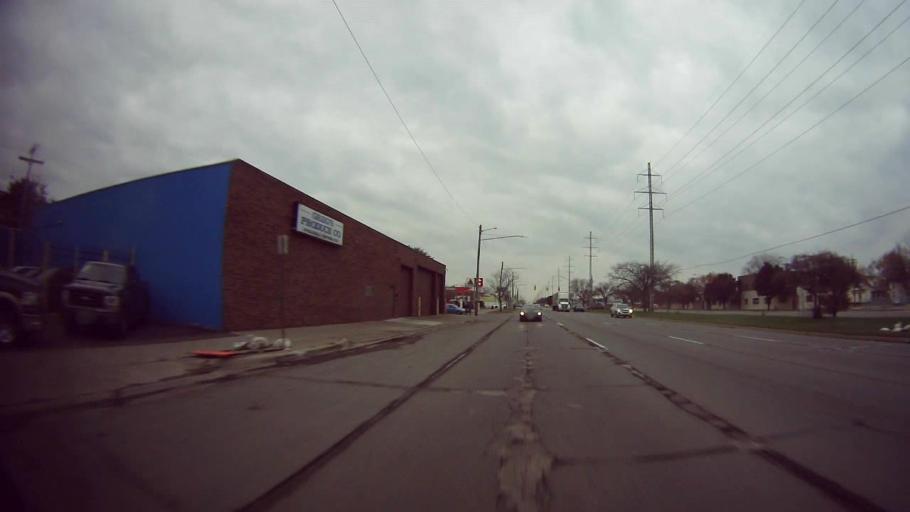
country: US
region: Michigan
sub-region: Macomb County
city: Eastpointe
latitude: 42.4495
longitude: -82.9751
